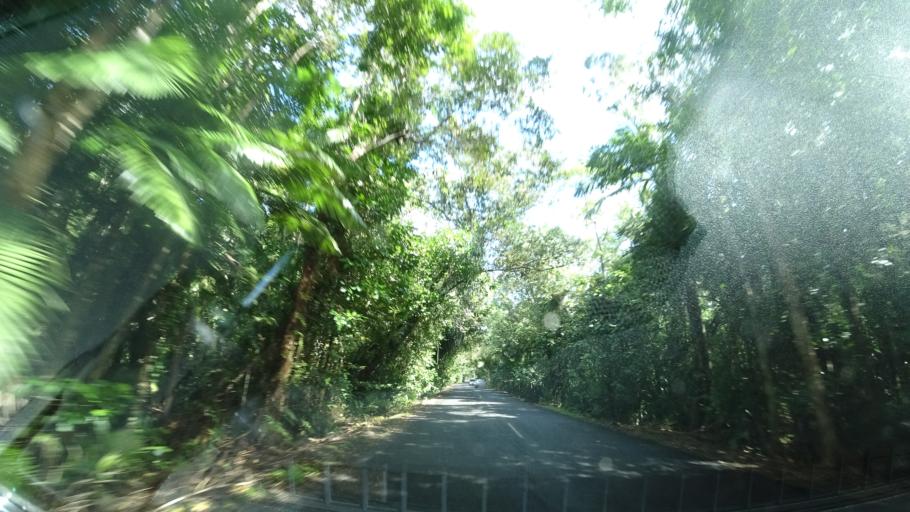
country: AU
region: Queensland
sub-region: Cairns
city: Port Douglas
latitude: -16.2538
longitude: 145.4074
